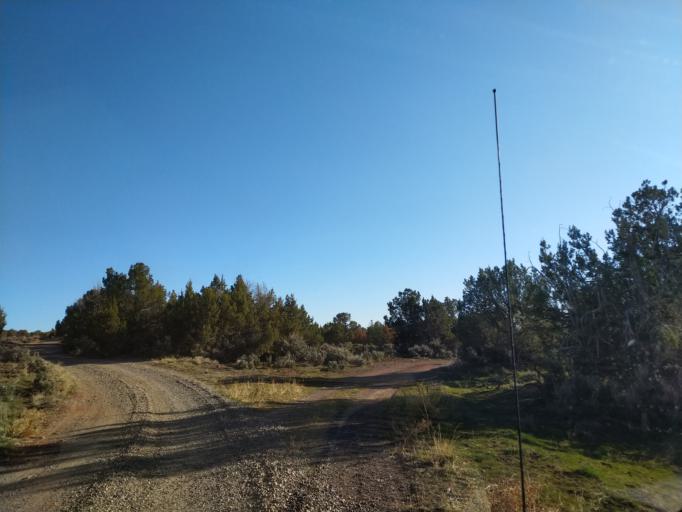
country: US
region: Colorado
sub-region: Mesa County
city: Loma
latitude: 38.9529
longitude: -109.0612
